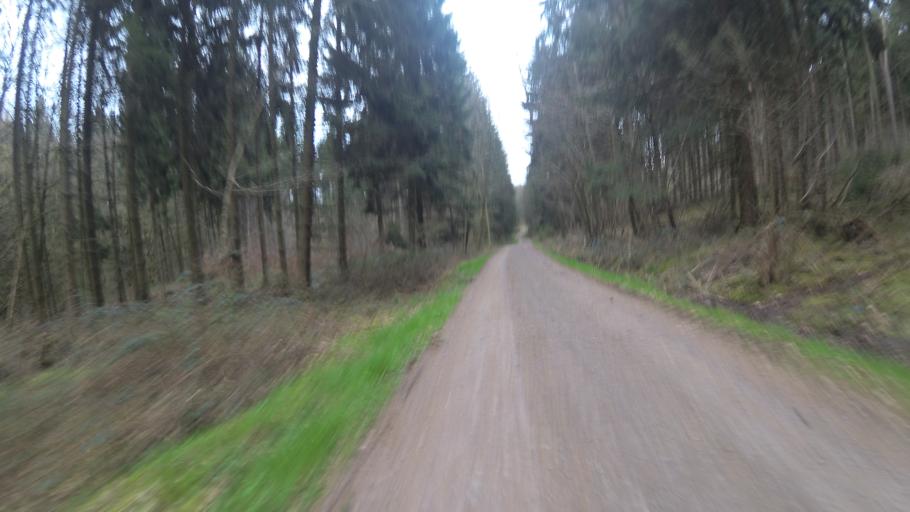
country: DE
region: Saarland
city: Sankt Wendel
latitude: 49.4367
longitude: 7.2111
